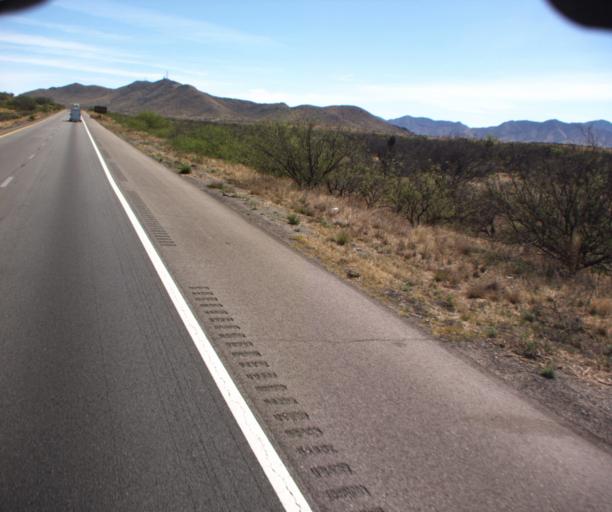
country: US
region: Arizona
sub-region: Cochise County
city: Saint David
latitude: 32.0067
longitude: -110.1373
